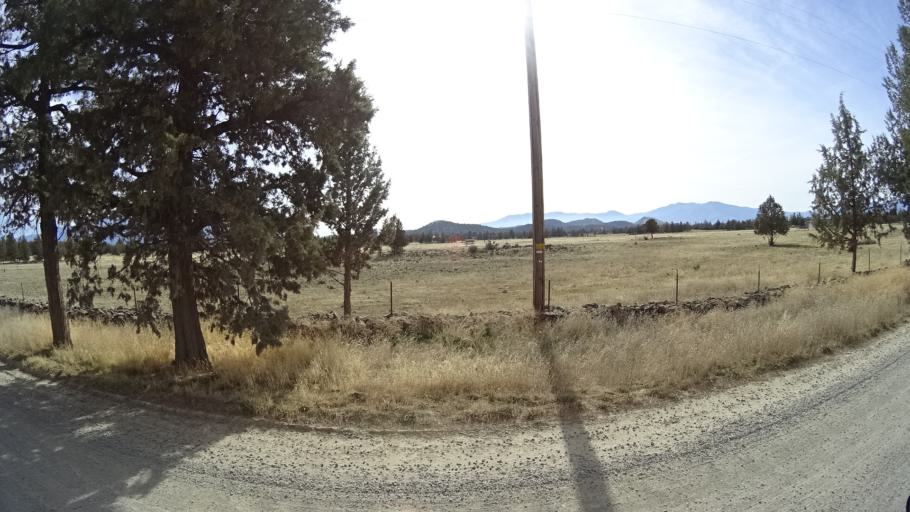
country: US
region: California
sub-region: Siskiyou County
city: Weed
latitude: 41.5955
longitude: -122.4046
